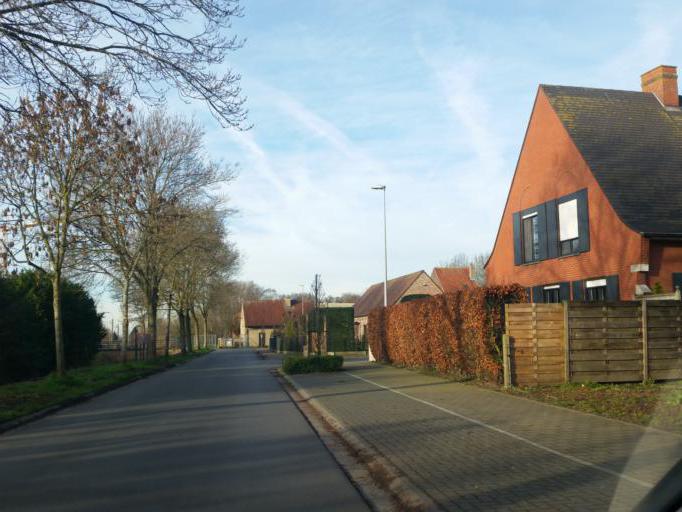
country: BE
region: Flanders
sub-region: Provincie Oost-Vlaanderen
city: Eeklo
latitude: 51.1761
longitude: 3.5702
